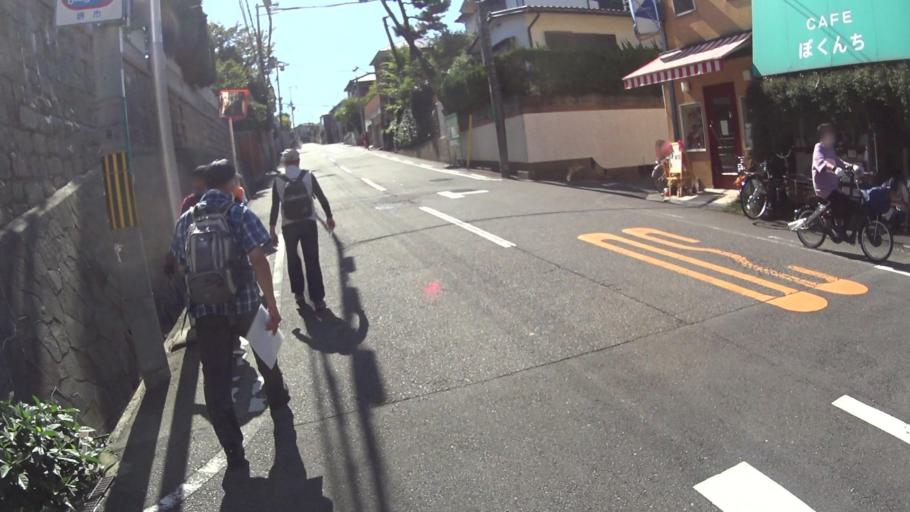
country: JP
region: Osaka
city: Takaishi
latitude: 34.5029
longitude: 135.4396
